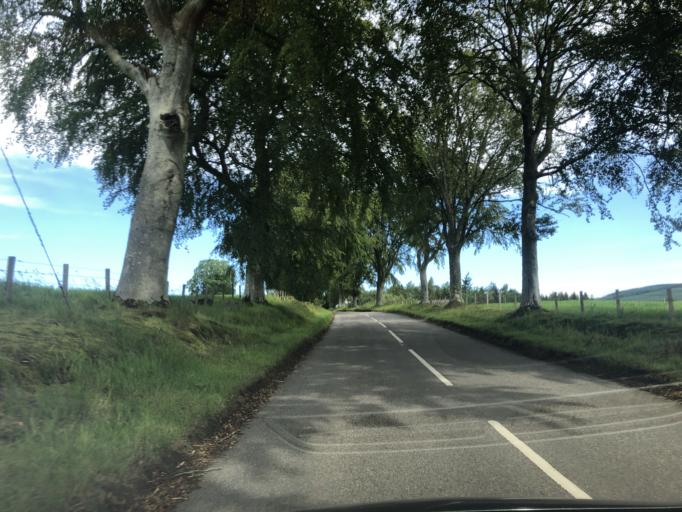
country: GB
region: Scotland
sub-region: Angus
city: Kirriemuir
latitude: 56.7263
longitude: -3.0026
